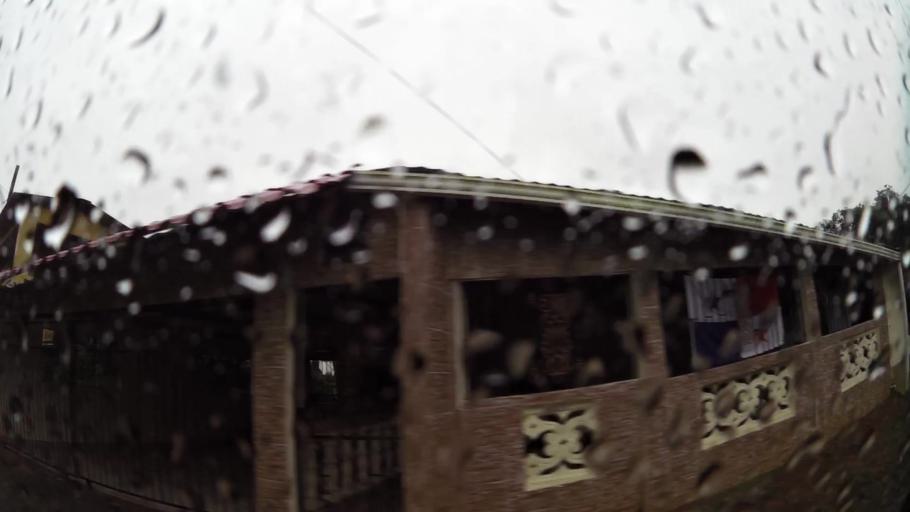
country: PA
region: Colon
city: Sabanitas
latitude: 9.3474
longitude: -79.7997
